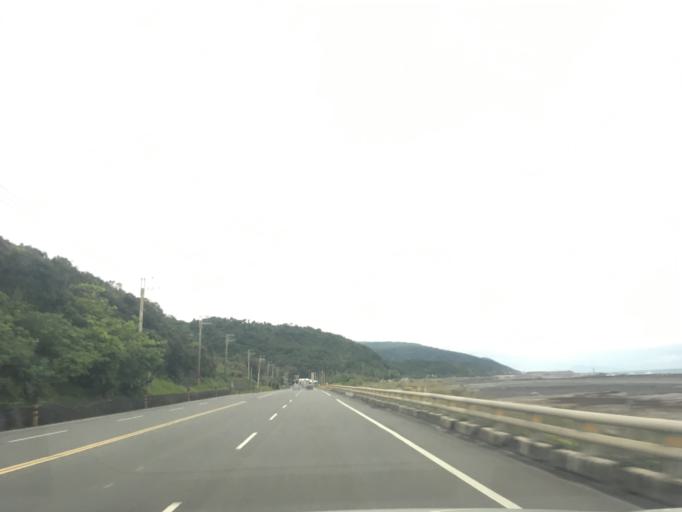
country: TW
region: Taiwan
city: Hengchun
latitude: 22.3258
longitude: 120.8922
